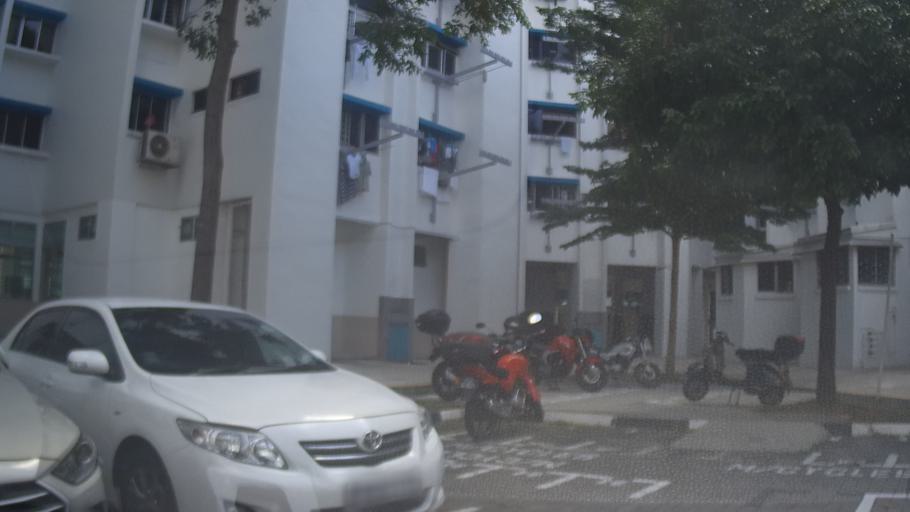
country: SG
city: Singapore
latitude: 1.3183
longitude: 103.8876
